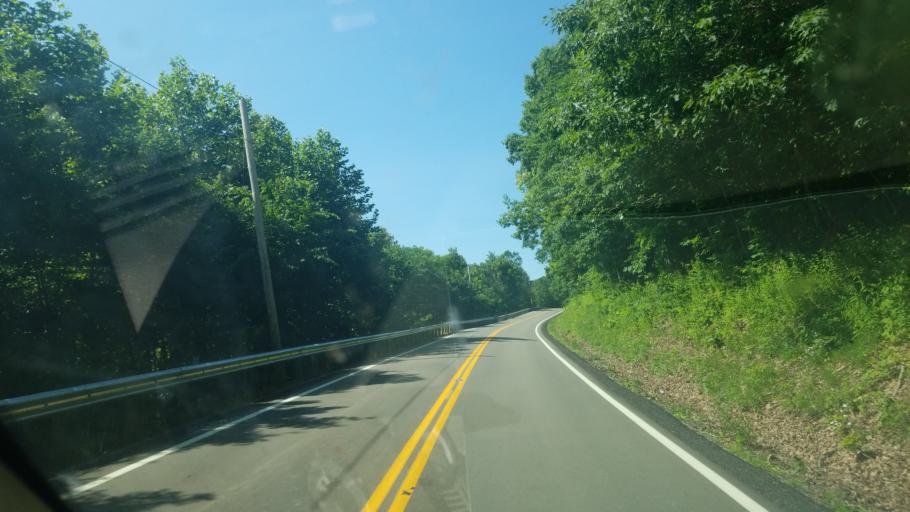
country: US
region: Ohio
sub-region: Holmes County
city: Millersburg
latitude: 40.4656
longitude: -81.9780
